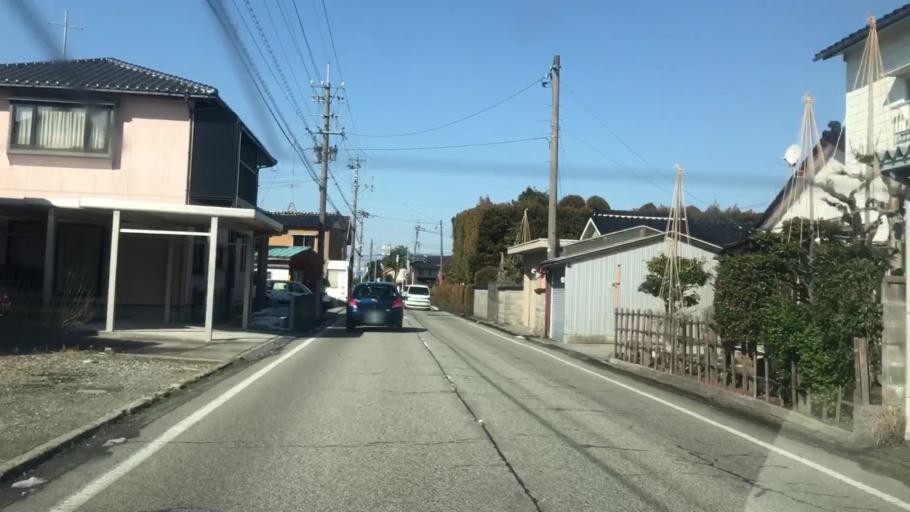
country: JP
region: Toyama
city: Toyama-shi
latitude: 36.6668
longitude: 137.2396
